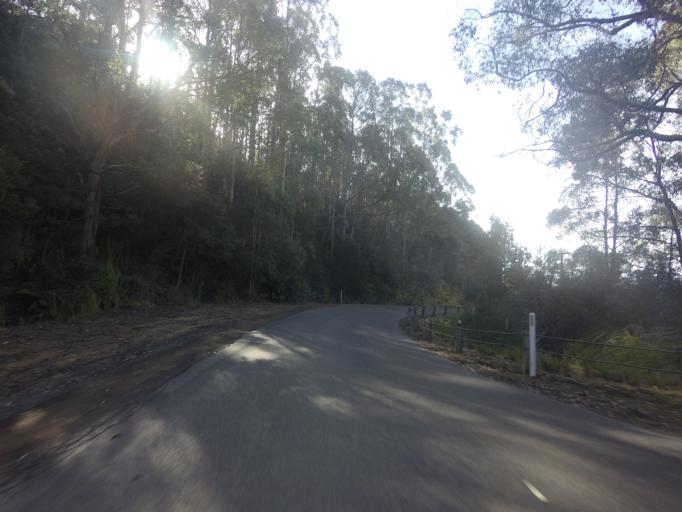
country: AU
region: Tasmania
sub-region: Kingborough
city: Kettering
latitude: -43.1701
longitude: 147.2035
